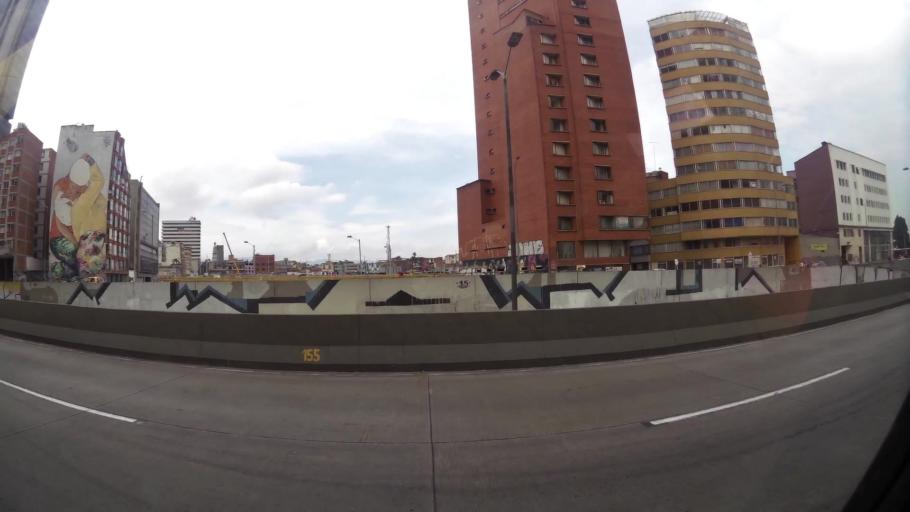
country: CO
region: Bogota D.C.
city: Bogota
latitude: 4.6143
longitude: -74.0719
